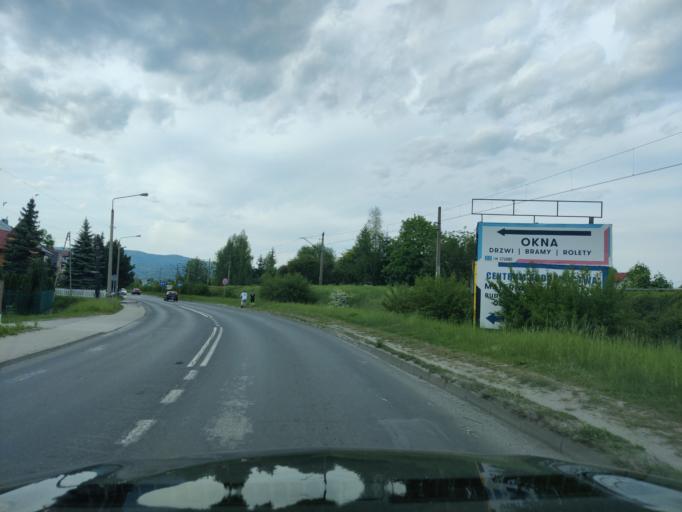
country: PL
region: Silesian Voivodeship
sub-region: Powiat zywiecki
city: Zywiec
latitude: 49.6832
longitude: 19.1871
